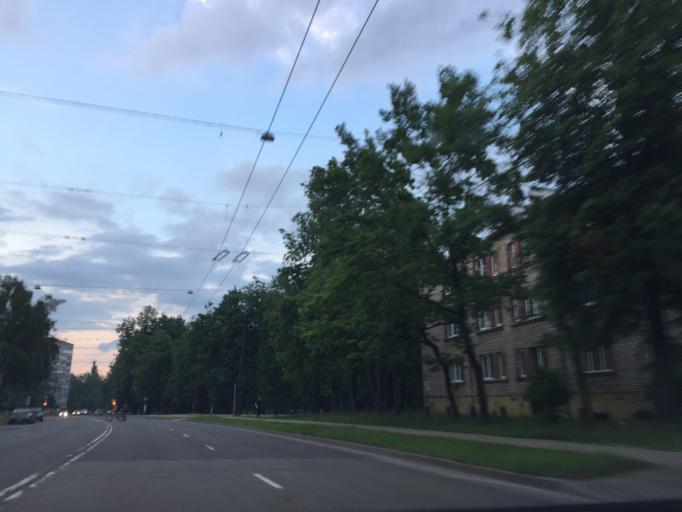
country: LV
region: Riga
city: Riga
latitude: 56.9623
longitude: 24.0546
